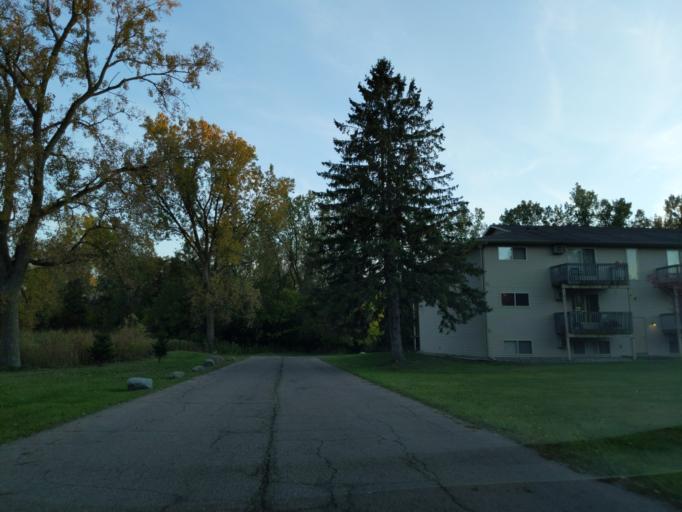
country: US
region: Michigan
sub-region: Ingham County
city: Edgemont Park
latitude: 42.7310
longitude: -84.5948
